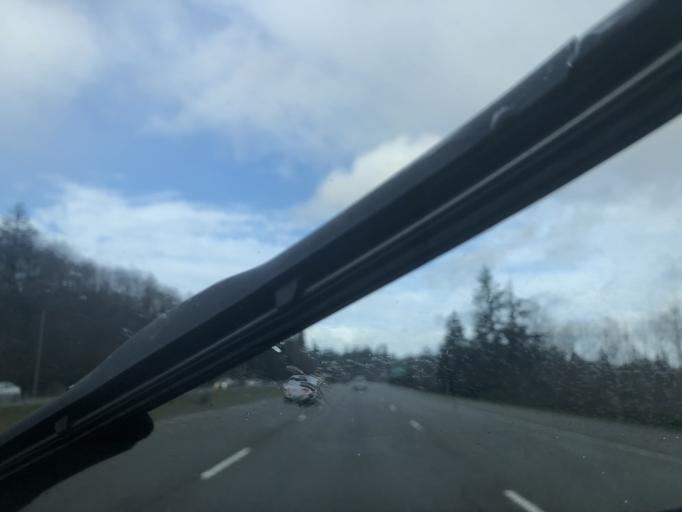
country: US
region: Washington
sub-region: Kitsap County
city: Silverdale
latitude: 47.6722
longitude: -122.6893
